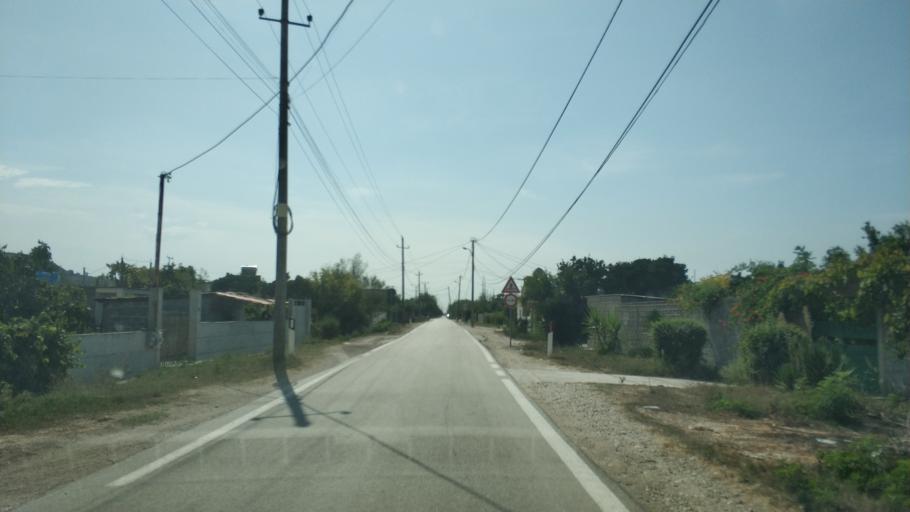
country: AL
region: Fier
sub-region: Rrethi i Fierit
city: Dermenas
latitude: 40.7382
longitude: 19.4776
